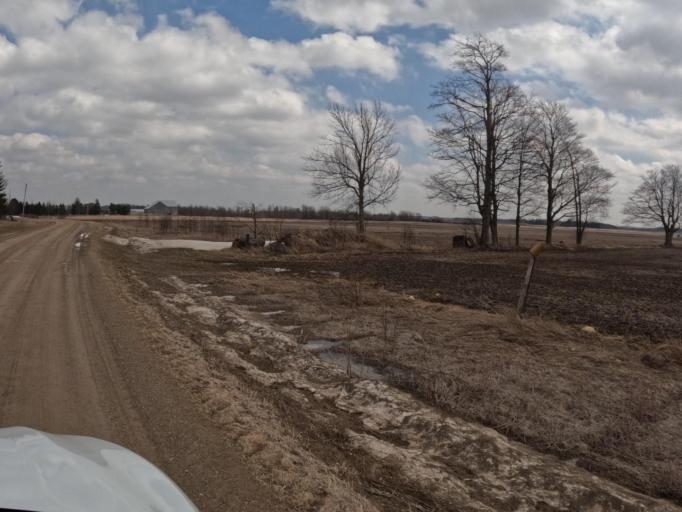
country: CA
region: Ontario
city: Shelburne
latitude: 44.0260
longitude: -80.2709
